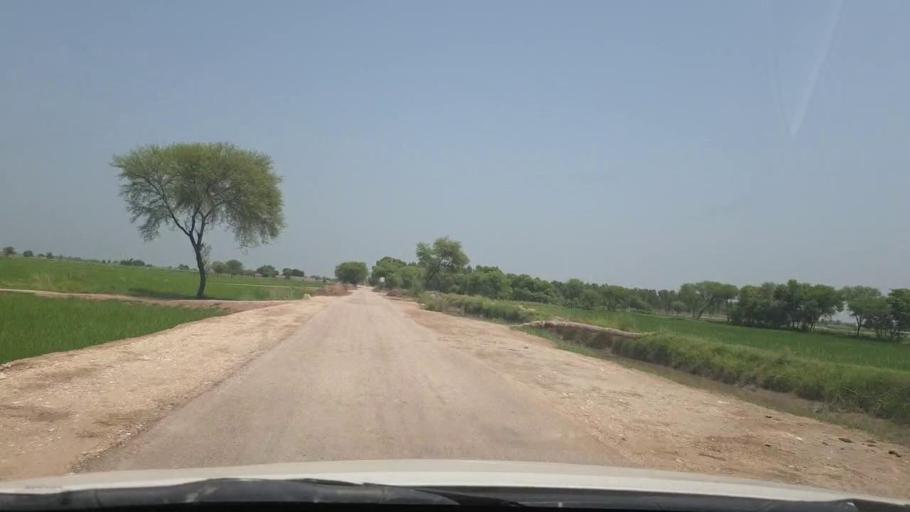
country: PK
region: Sindh
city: Rustam jo Goth
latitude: 28.0287
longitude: 68.7764
